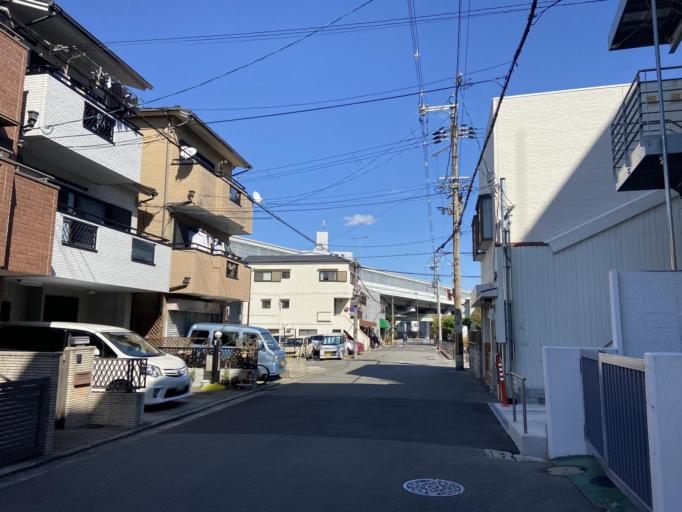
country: JP
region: Osaka
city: Sakai
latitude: 34.5632
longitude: 135.4656
